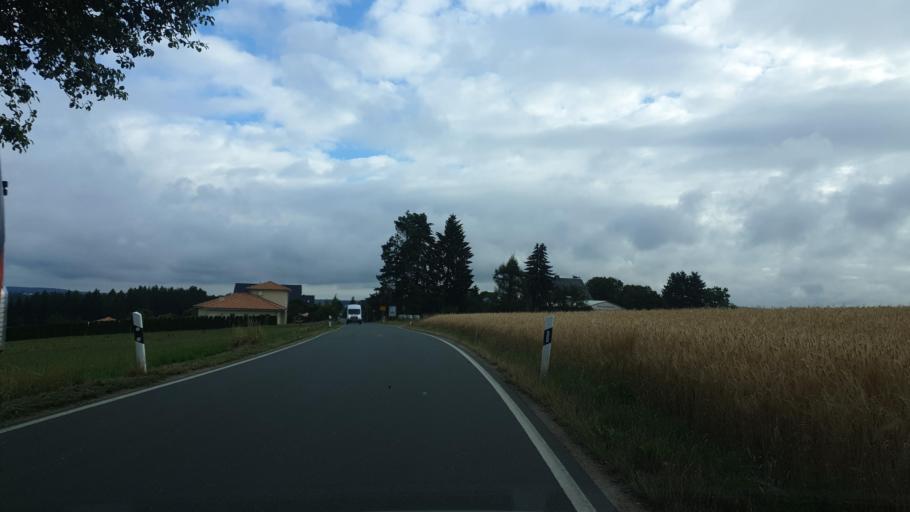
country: DE
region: Saxony
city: Netzschkau
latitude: 50.5999
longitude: 12.2411
